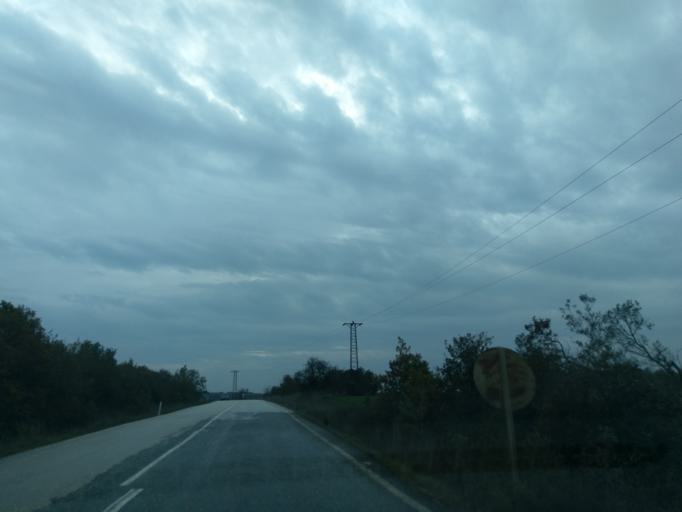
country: TR
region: Istanbul
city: Canta
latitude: 41.1745
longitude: 28.0910
